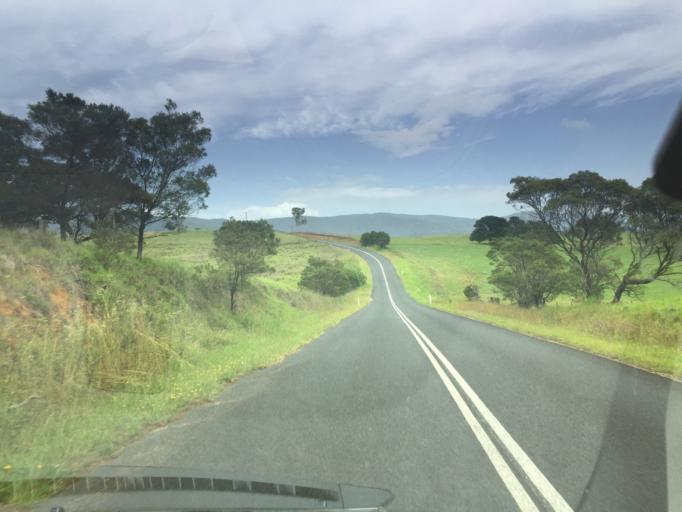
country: AU
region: New South Wales
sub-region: Bega Valley
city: Bega
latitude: -36.7284
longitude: 149.6237
